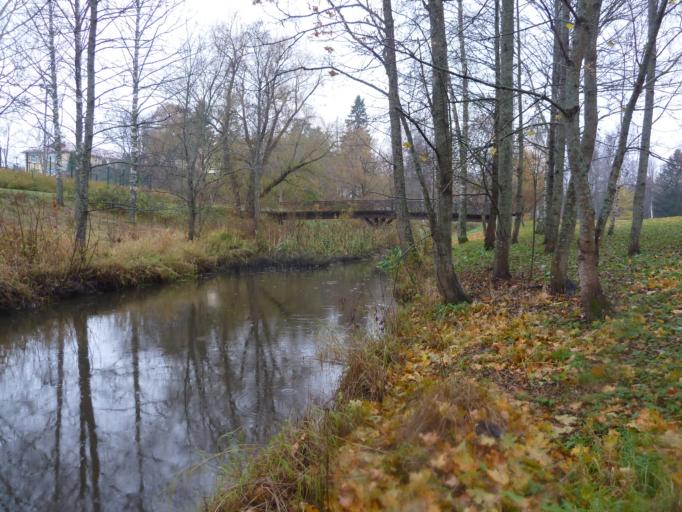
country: FI
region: Uusimaa
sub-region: Helsinki
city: Espoo
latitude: 60.2088
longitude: 24.6559
